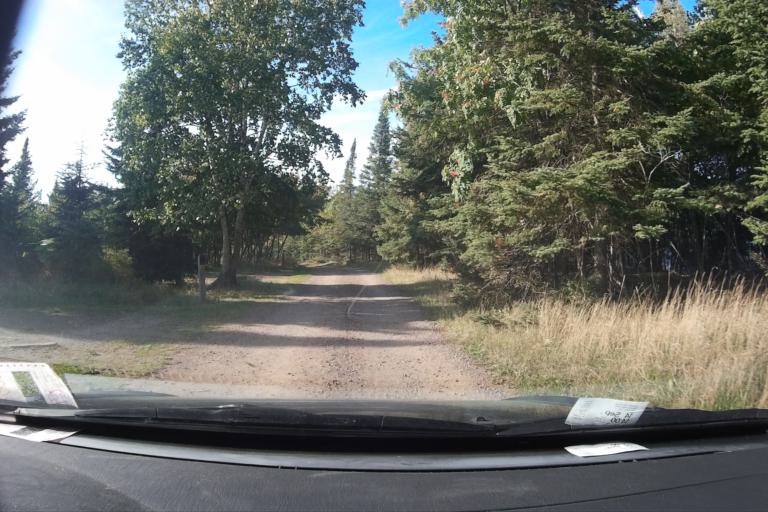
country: CA
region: Ontario
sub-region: Thunder Bay District
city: Thunder Bay
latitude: 48.3716
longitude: -88.8065
